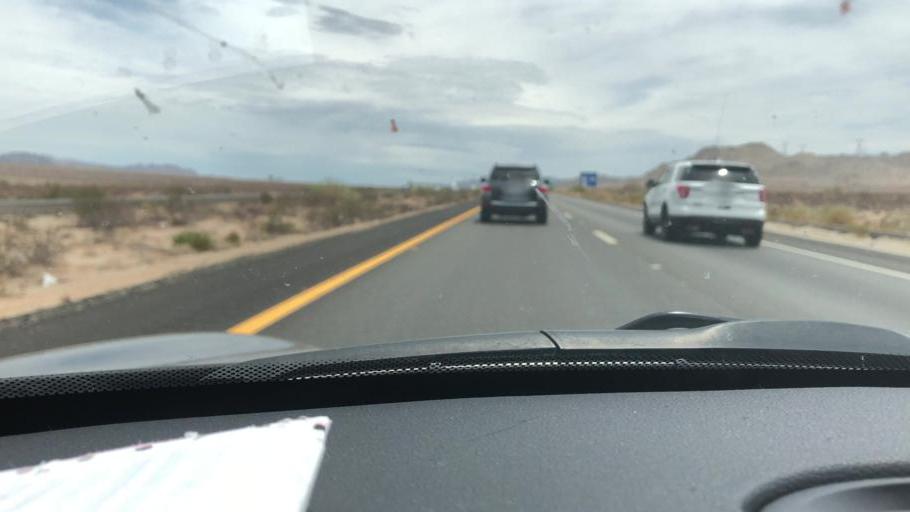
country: US
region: California
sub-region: Riverside County
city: Mecca
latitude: 33.6599
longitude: -115.7478
